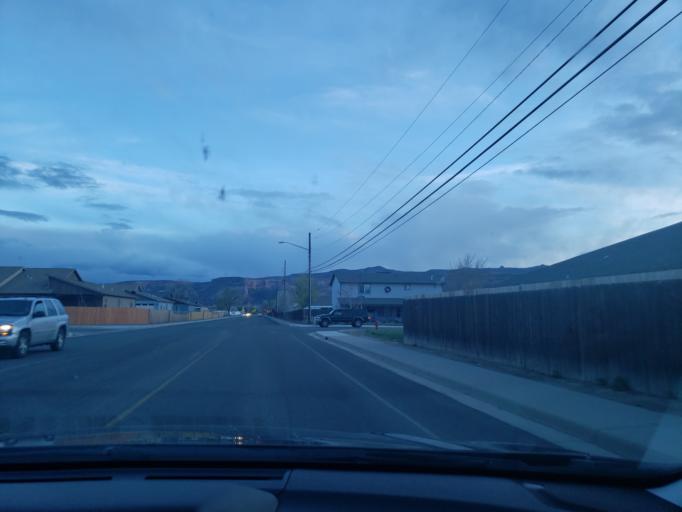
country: US
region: Colorado
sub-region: Mesa County
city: Fruita
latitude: 39.1529
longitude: -108.7198
